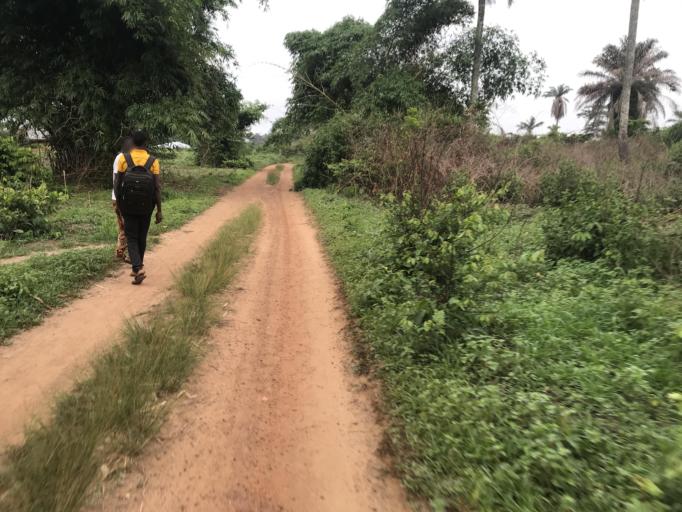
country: SL
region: Eastern Province
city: Pendembu
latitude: 8.0903
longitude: -10.6940
